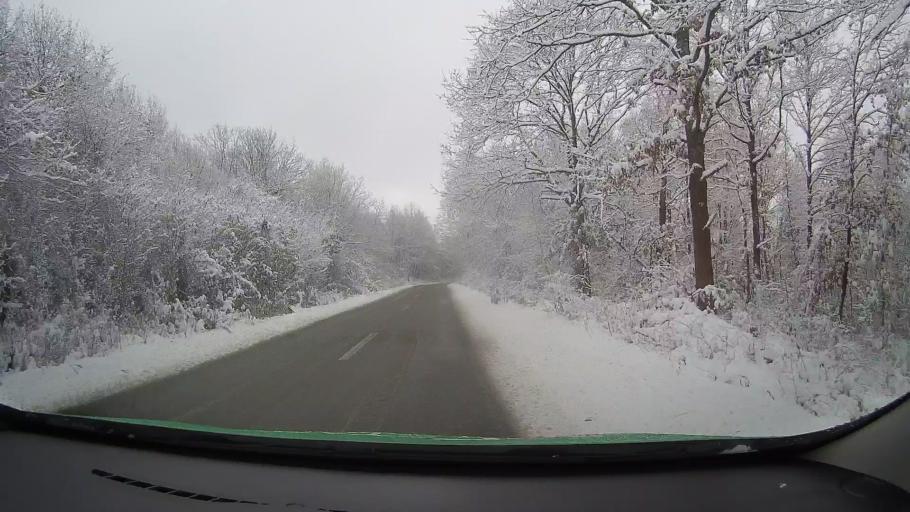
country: RO
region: Hunedoara
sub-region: Comuna Teliucu Inferior
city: Teliucu Inferior
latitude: 45.6750
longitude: 22.9144
